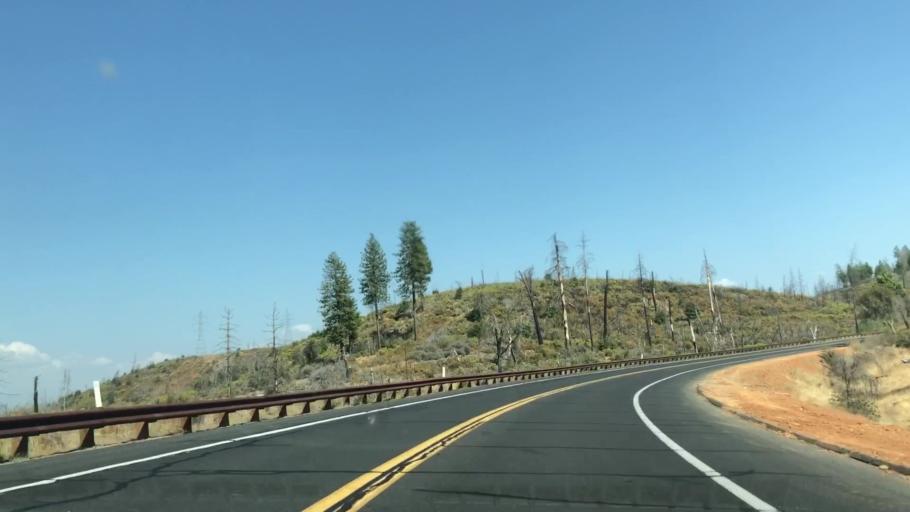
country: US
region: California
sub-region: Tuolumne County
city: Tuolumne City
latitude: 37.8255
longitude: -120.0926
